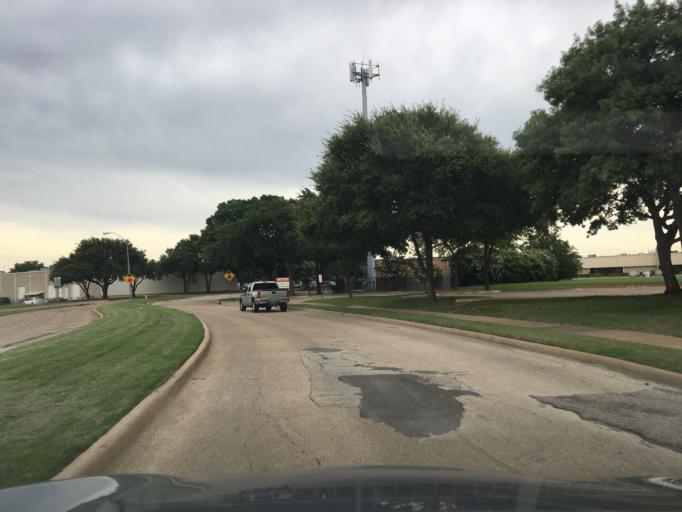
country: US
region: Texas
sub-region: Dallas County
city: Richardson
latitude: 32.9672
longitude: -96.7062
